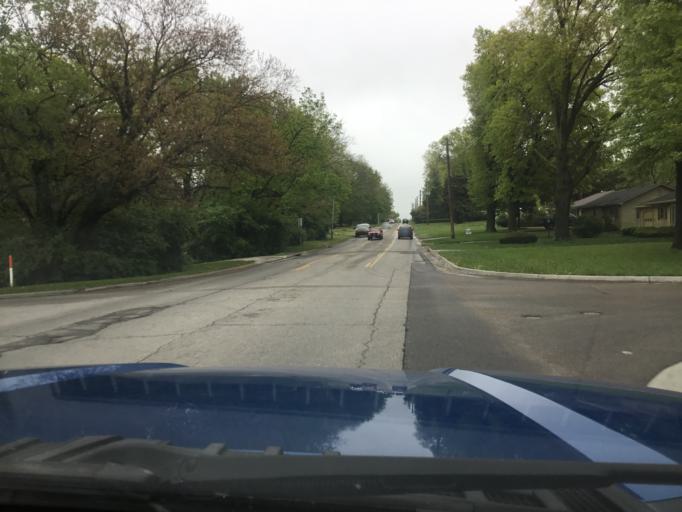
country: US
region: Kansas
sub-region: Shawnee County
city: Topeka
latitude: 39.0367
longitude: -95.7306
